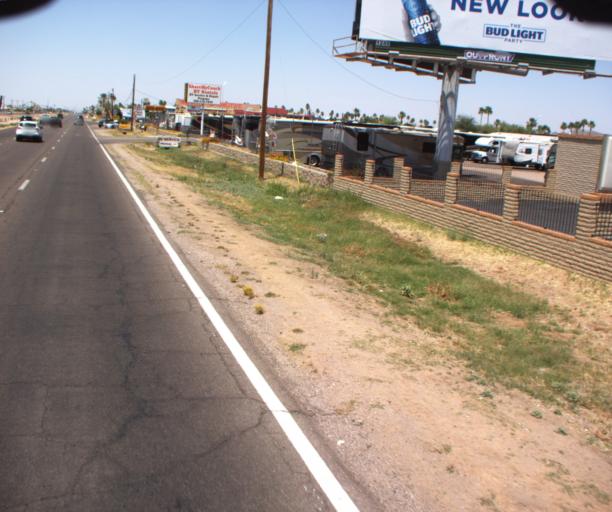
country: US
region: Arizona
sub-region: Pinal County
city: Apache Junction
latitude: 33.4154
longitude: -111.5860
